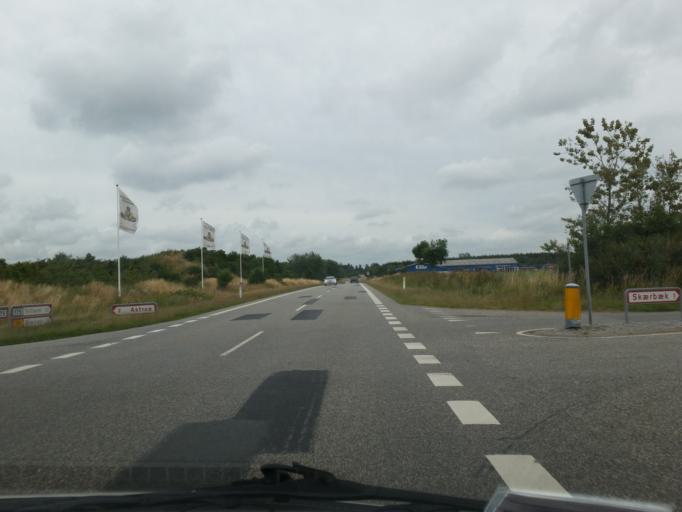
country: DK
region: South Denmark
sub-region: Tonder Kommune
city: Sherrebek
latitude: 55.1665
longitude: 8.7473
